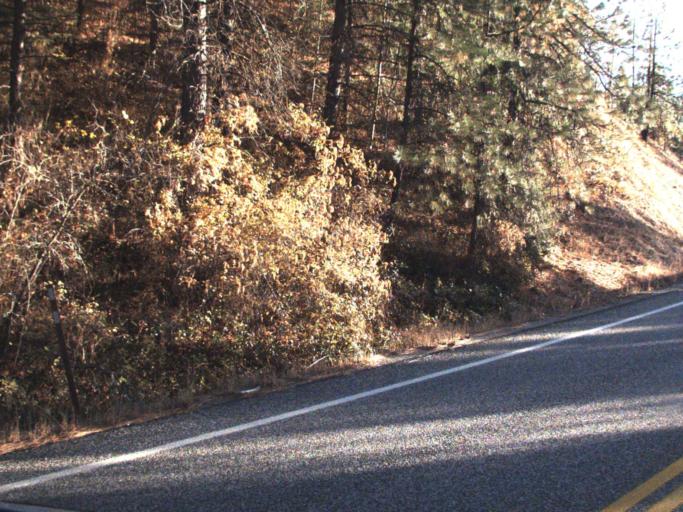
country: US
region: Washington
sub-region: Stevens County
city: Kettle Falls
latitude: 48.8033
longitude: -118.0045
